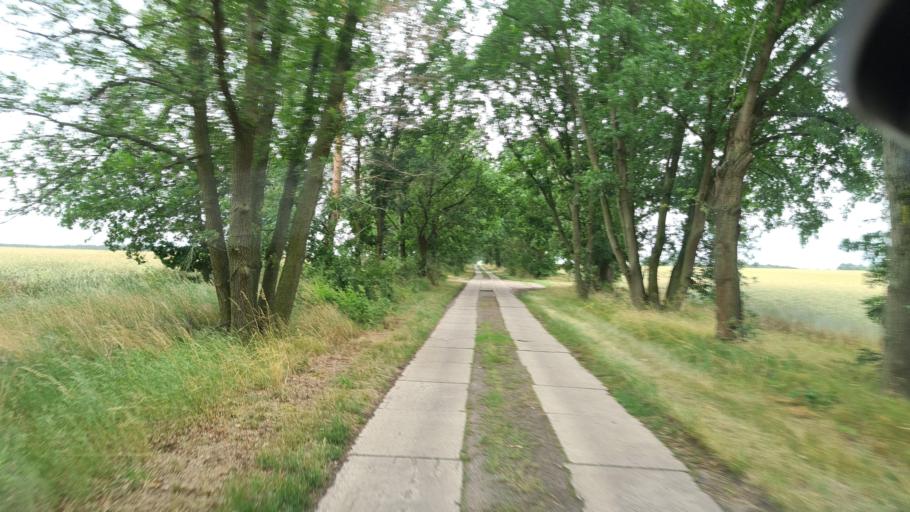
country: DE
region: Brandenburg
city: Juterbog
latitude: 51.9675
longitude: 13.1705
